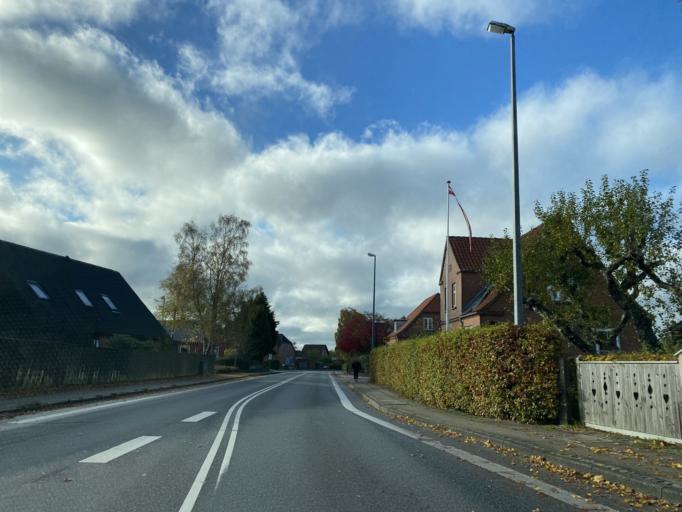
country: DK
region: Central Jutland
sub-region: Favrskov Kommune
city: Hammel
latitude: 56.2584
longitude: 9.8670
